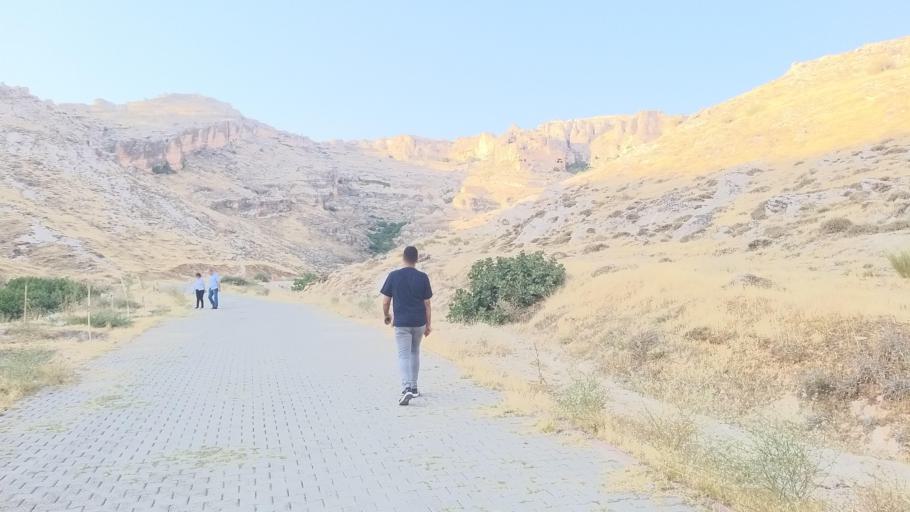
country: TR
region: Diyarbakir
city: Silvan
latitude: 38.1316
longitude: 41.0885
